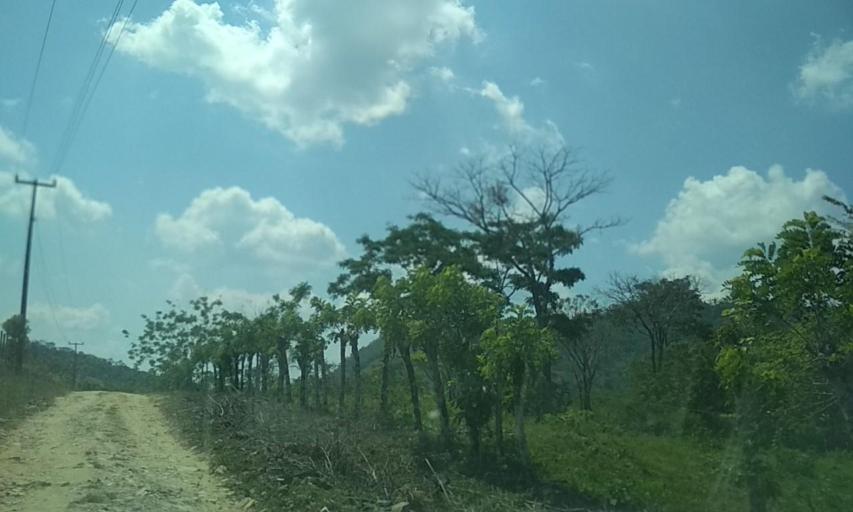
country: MX
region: Chiapas
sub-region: Tecpatan
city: Raudales Malpaso
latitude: 17.2993
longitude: -93.8127
